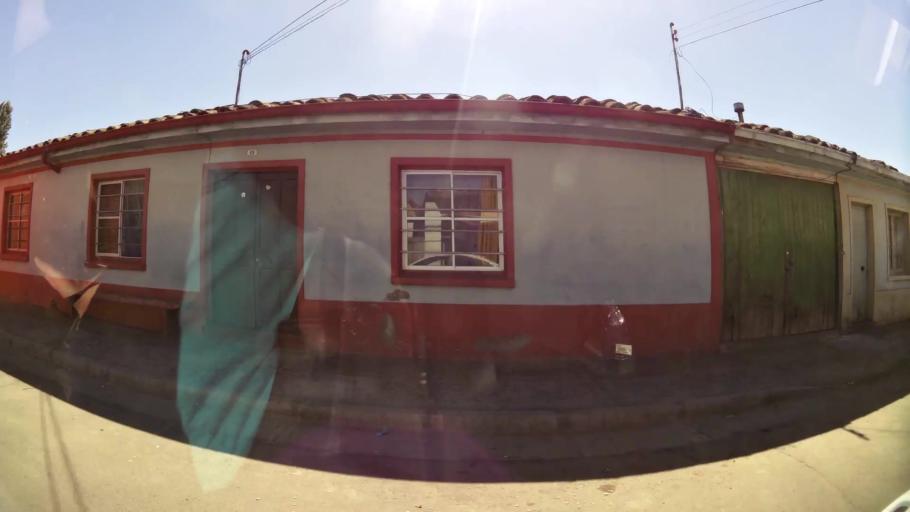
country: CL
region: O'Higgins
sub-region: Provincia de Colchagua
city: Chimbarongo
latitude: -34.5927
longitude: -70.9963
